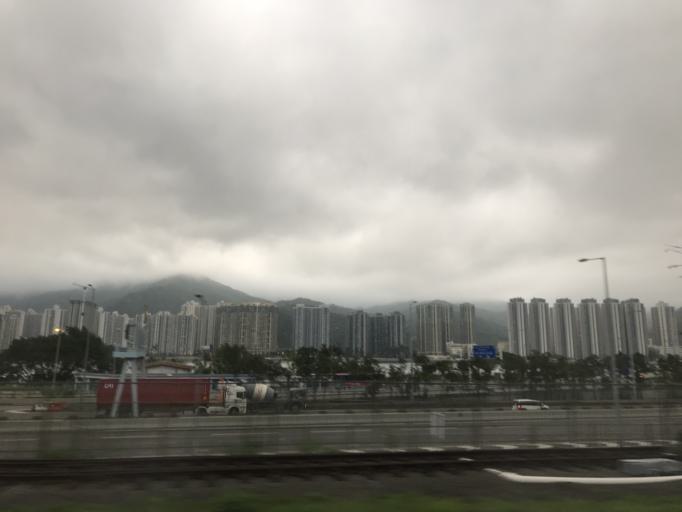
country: HK
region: Sha Tin
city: Sha Tin
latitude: 22.4171
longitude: 114.2129
